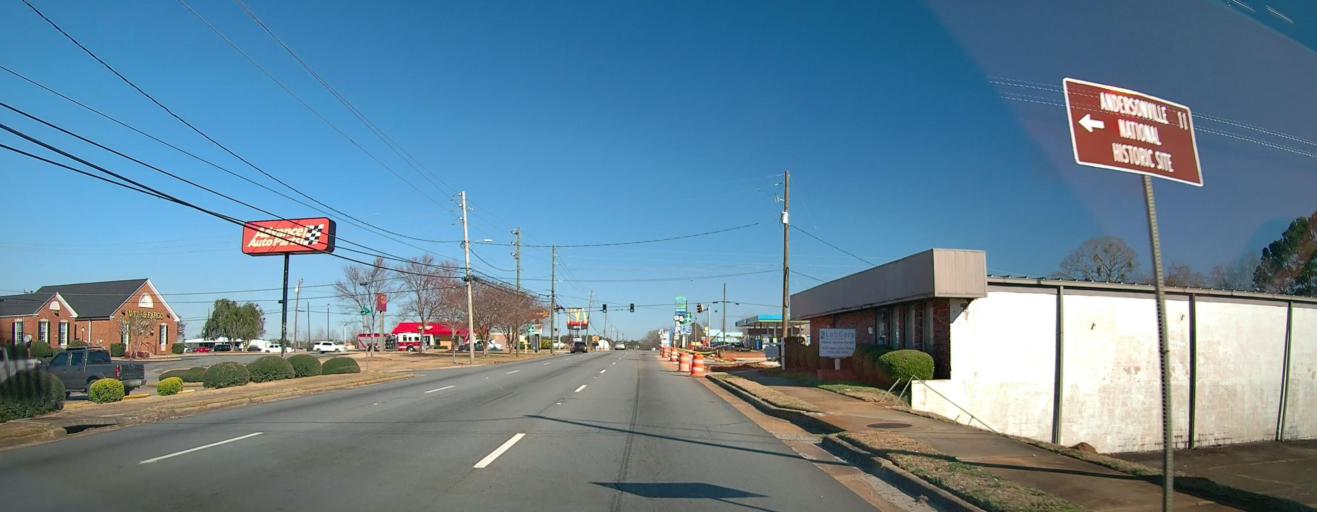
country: US
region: Georgia
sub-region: Sumter County
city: Americus
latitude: 32.0713
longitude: -84.2186
